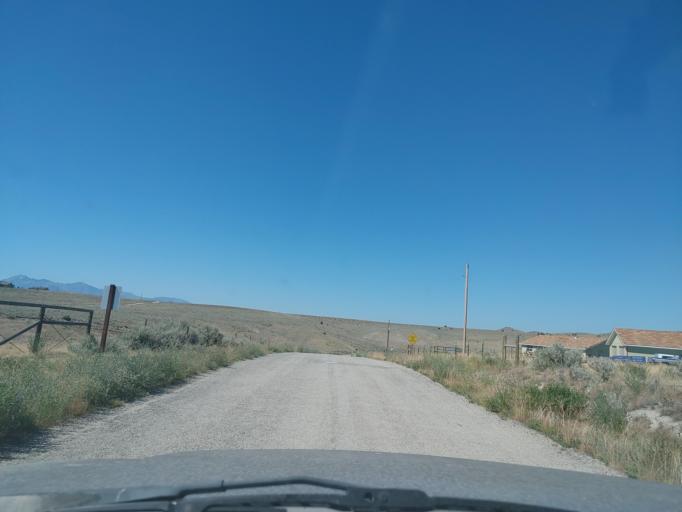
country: US
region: Montana
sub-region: Ravalli County
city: Stevensville
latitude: 46.3581
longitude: -114.0378
